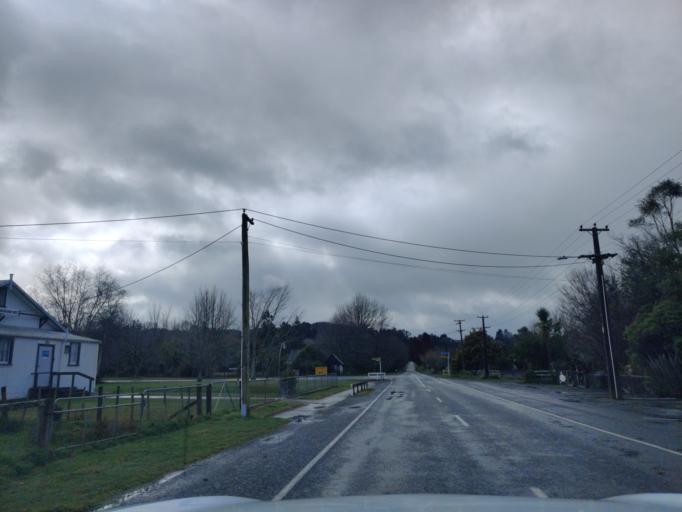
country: NZ
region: Manawatu-Wanganui
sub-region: Palmerston North City
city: Palmerston North
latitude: -40.1741
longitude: 175.7942
